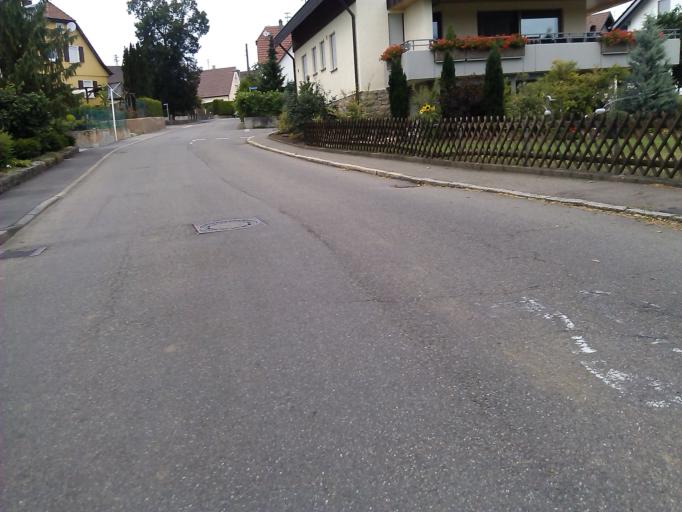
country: DE
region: Baden-Wuerttemberg
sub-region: Regierungsbezirk Stuttgart
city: Oedheim
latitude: 49.2417
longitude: 9.2498
